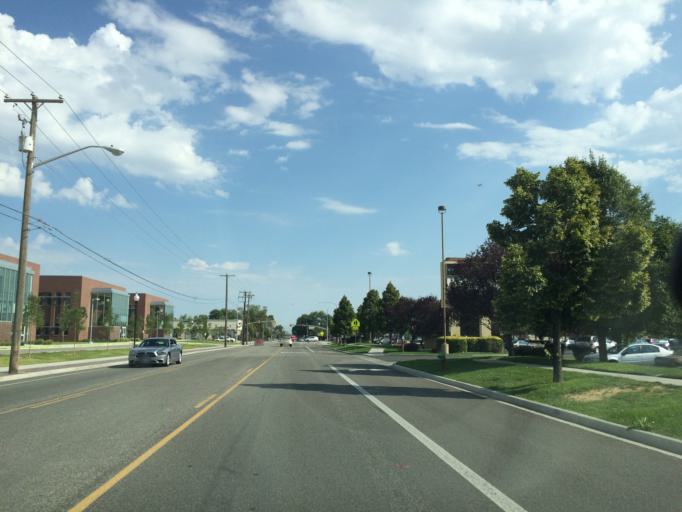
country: US
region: Utah
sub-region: Salt Lake County
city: West Valley City
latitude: 40.6947
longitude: -111.9772
